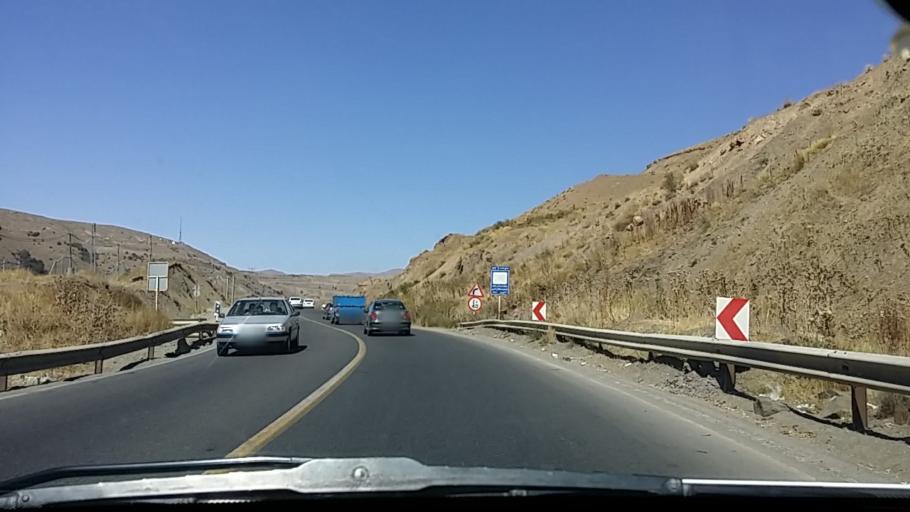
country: IR
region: Tehran
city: Tajrish
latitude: 36.1883
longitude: 51.3203
